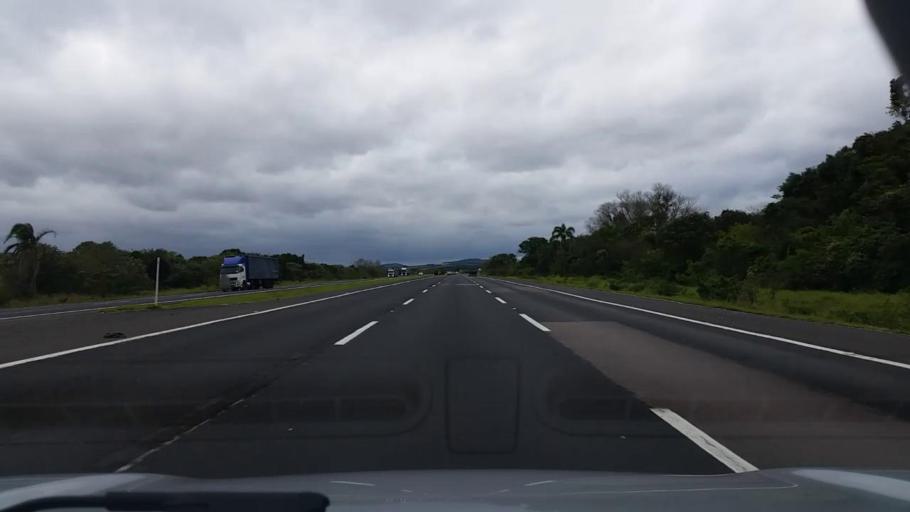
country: BR
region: Rio Grande do Sul
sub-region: Osorio
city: Osorio
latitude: -29.8775
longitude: -50.4286
